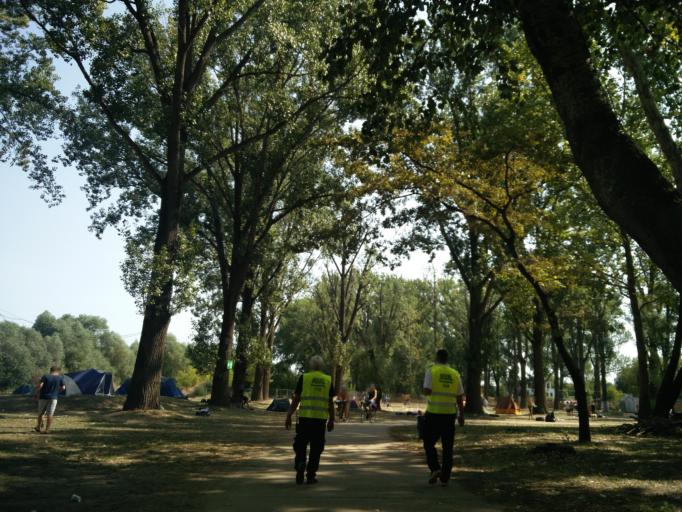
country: HU
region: Csongrad
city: Szeged
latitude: 46.2541
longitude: 20.1610
